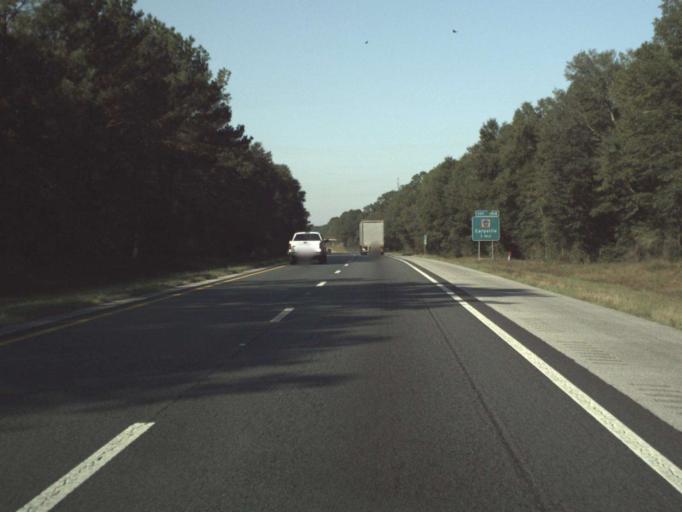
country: US
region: Florida
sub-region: Holmes County
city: Bonifay
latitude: 30.7613
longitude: -85.7912
